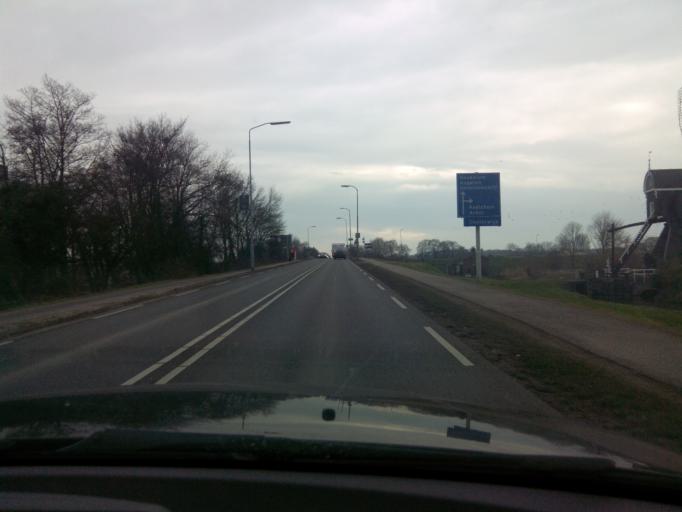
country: NL
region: South Holland
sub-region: Gemeente Leerdam
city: Leerdam
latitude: 51.8909
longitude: 5.0895
